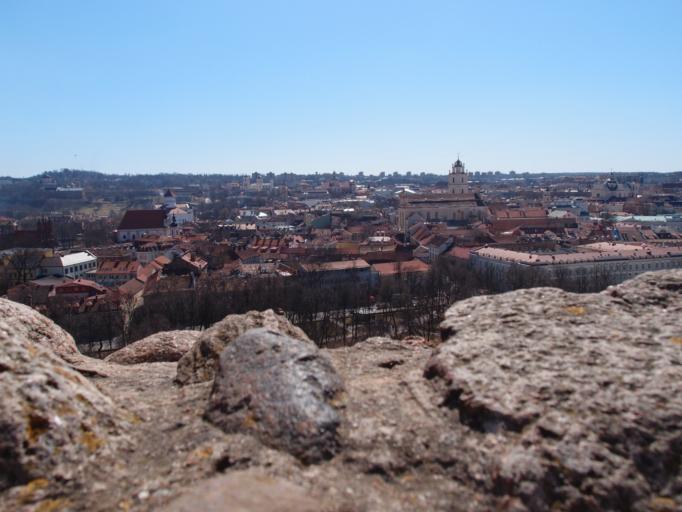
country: LT
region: Vilnius County
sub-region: Vilnius
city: Vilnius
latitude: 54.6865
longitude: 25.2909
